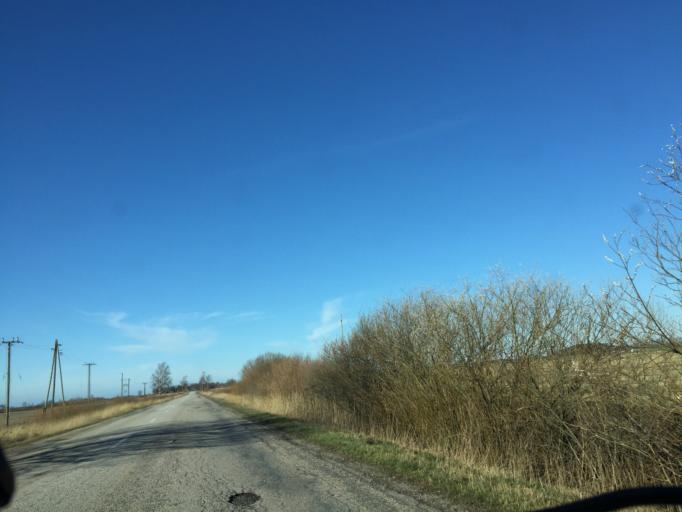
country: LV
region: Ventspils Rajons
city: Piltene
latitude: 57.3036
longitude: 21.6437
